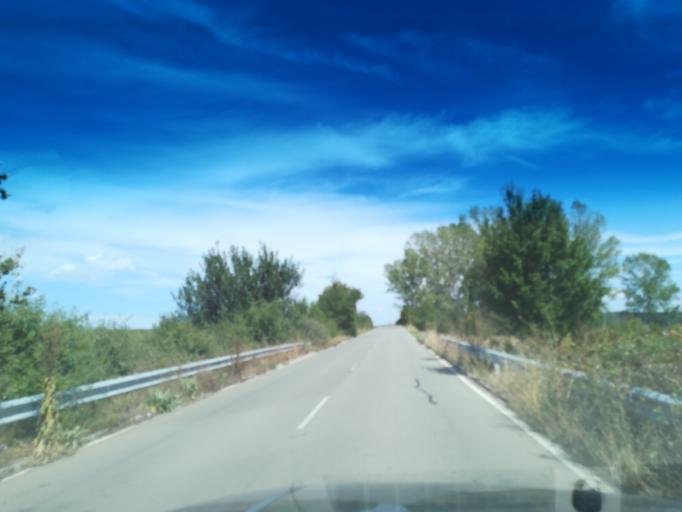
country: BG
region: Plovdiv
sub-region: Obshtina Suedinenie
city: Suedinenie
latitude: 42.4191
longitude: 24.5188
